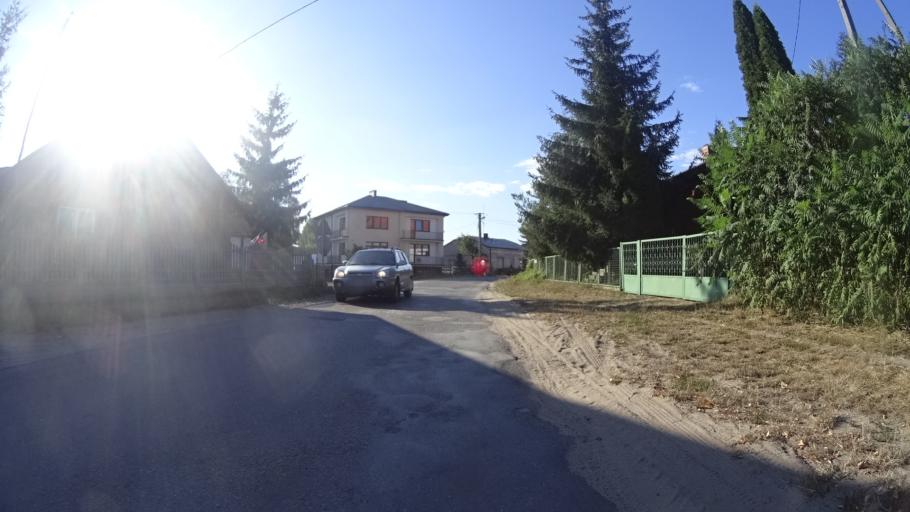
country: PL
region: Masovian Voivodeship
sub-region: Powiat bialobrzeski
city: Wysmierzyce
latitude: 51.6528
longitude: 20.7845
